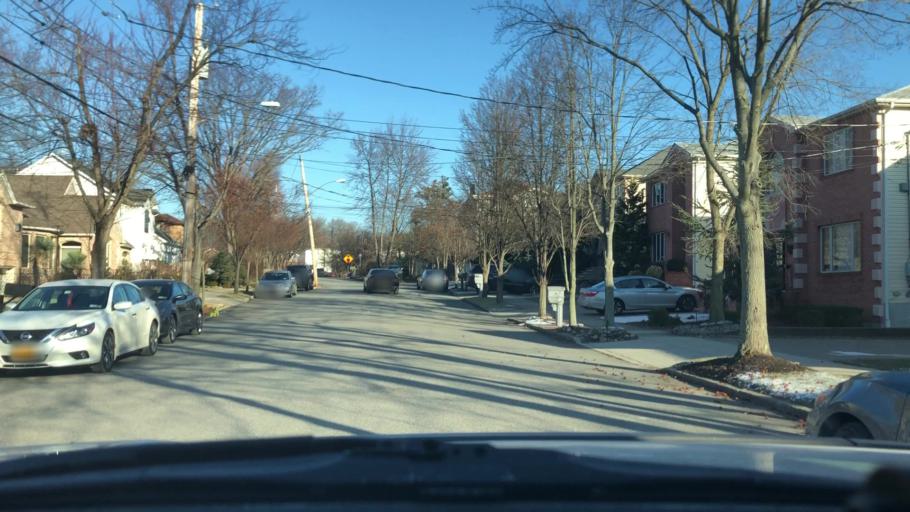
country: US
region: New Jersey
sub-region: Middlesex County
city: Carteret
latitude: 40.5195
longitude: -74.1991
